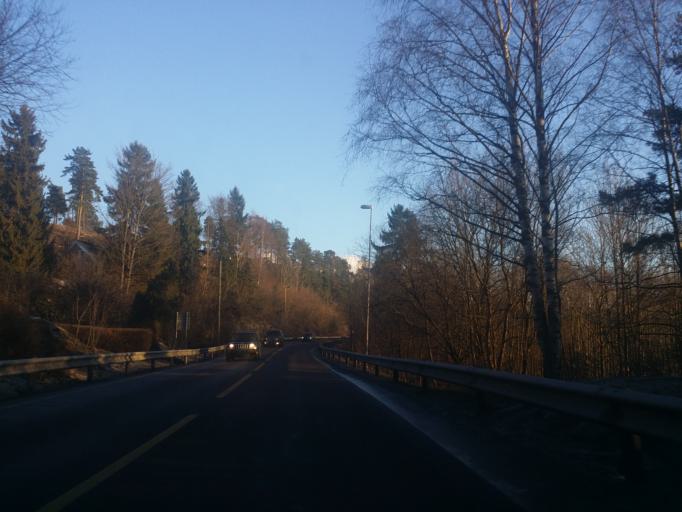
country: NO
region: Buskerud
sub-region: Ringerike
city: Honefoss
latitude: 60.1277
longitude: 10.2772
